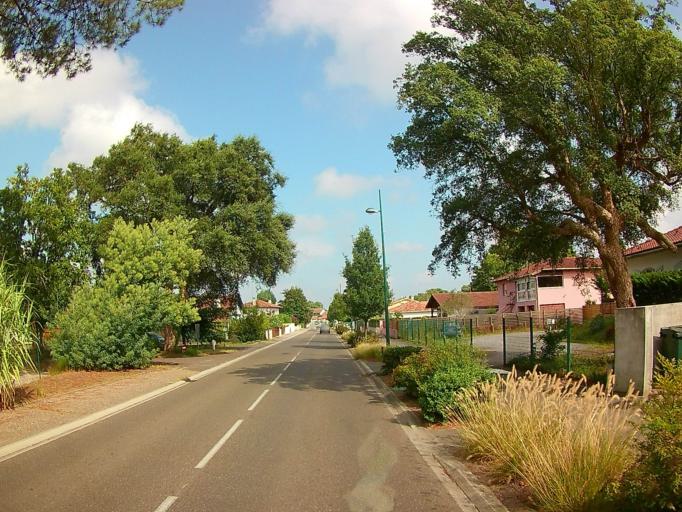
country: FR
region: Aquitaine
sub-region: Departement des Landes
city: Labenne
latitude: 43.5925
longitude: -1.4351
